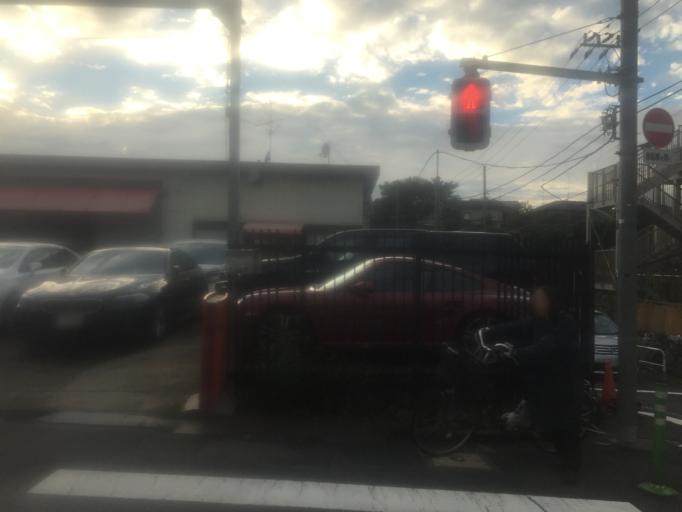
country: JP
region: Tokyo
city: Tokyo
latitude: 35.6031
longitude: 139.6653
